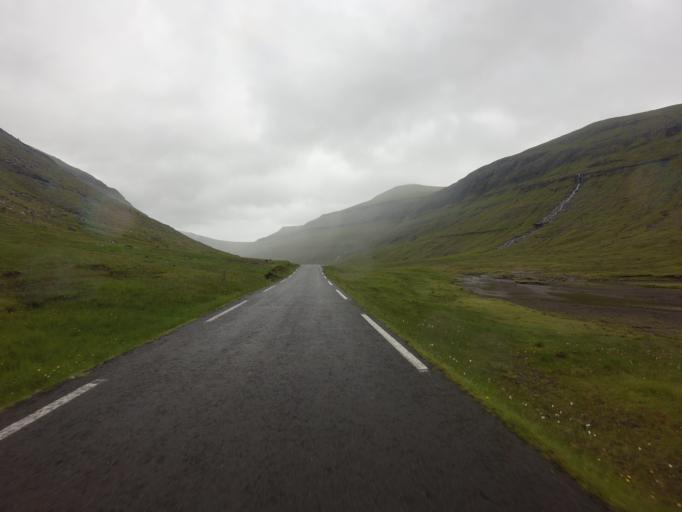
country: FO
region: Streymoy
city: Vestmanna
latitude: 62.2322
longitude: -7.1393
